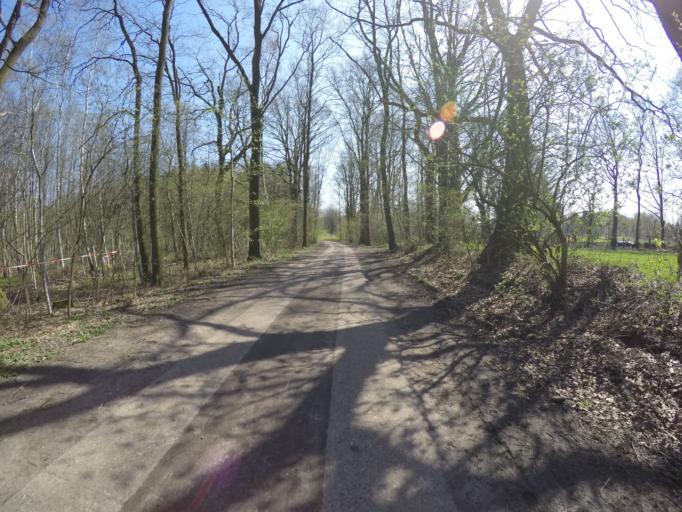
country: DE
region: Schleswig-Holstein
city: Ellerau
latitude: 53.7398
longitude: 9.9169
